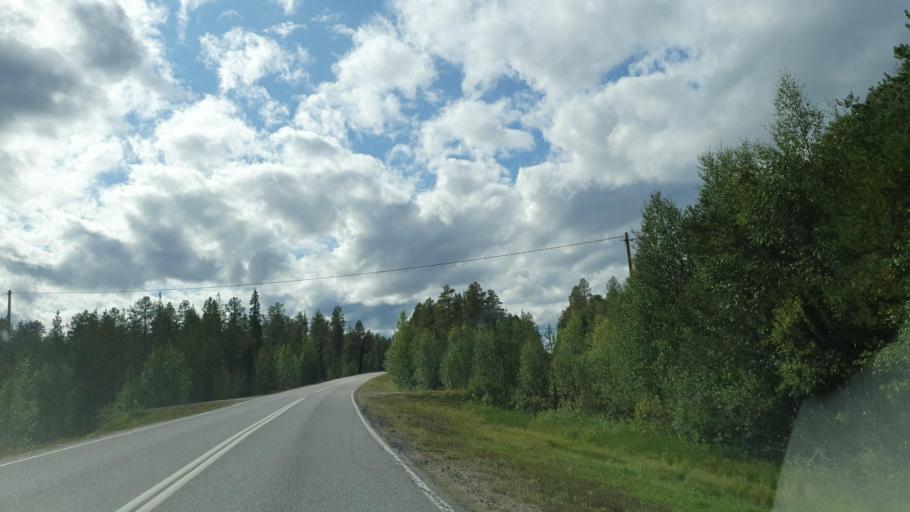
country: FI
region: Lapland
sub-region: Tunturi-Lappi
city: Muonio
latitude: 67.8754
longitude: 24.2035
